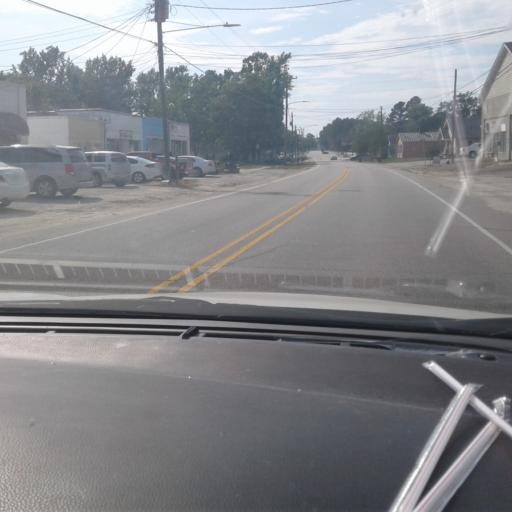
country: US
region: North Carolina
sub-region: Harnett County
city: Erwin
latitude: 35.3232
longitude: -78.6597
